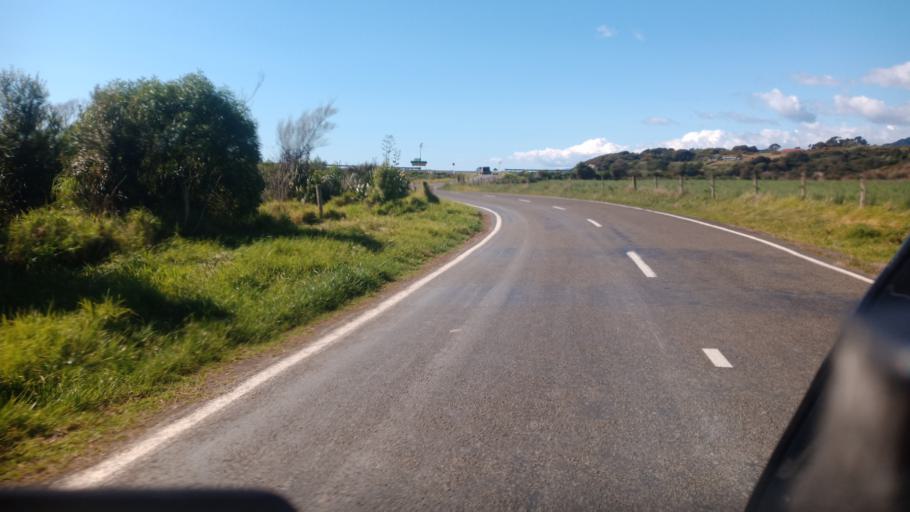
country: NZ
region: Bay of Plenty
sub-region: Opotiki District
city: Opotiki
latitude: -37.9904
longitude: 177.3889
